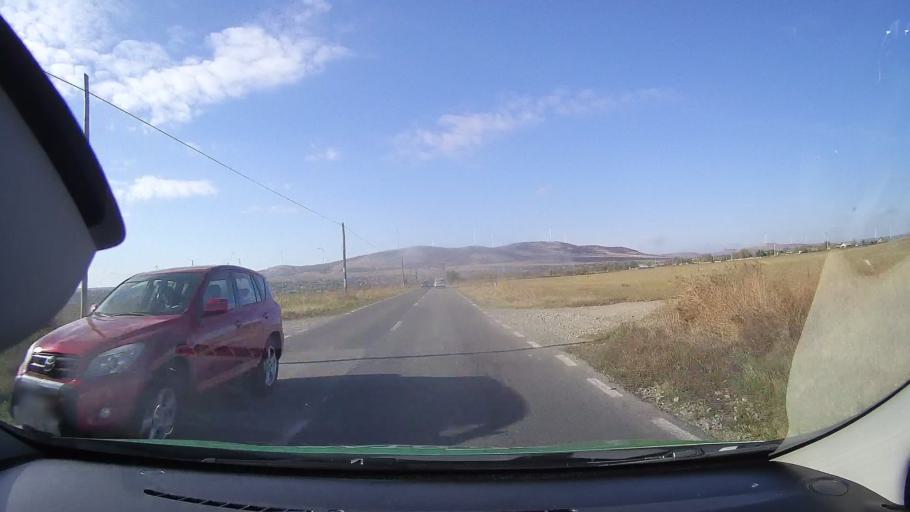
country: RO
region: Tulcea
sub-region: Comuna Valea Nucarilor
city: Agighiol
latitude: 45.0351
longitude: 28.8912
